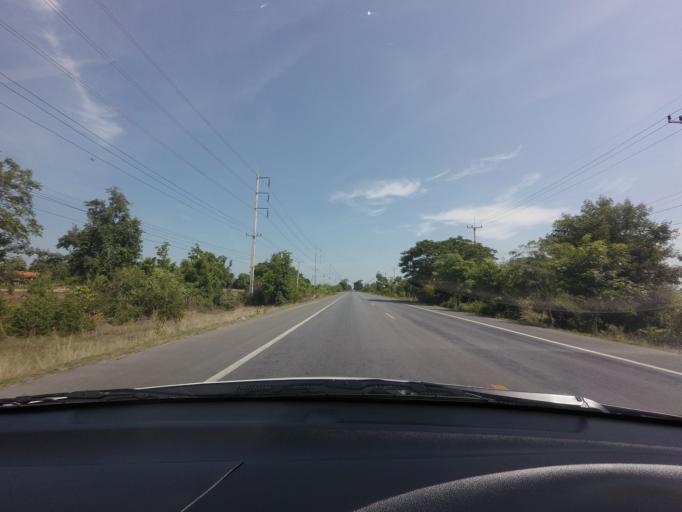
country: TH
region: Suphan Buri
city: Nong Yasai
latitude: 14.6962
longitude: 99.8428
